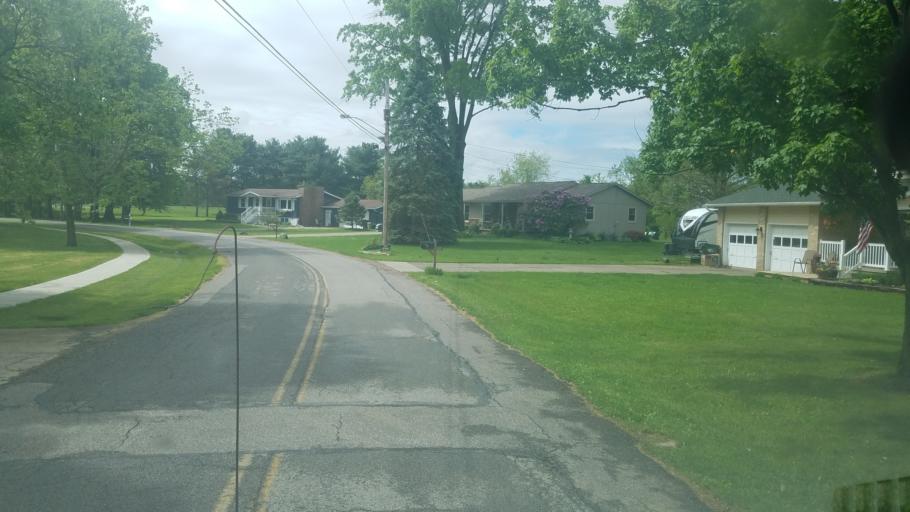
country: US
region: Ohio
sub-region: Wayne County
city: Smithville
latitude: 40.8546
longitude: -81.8642
